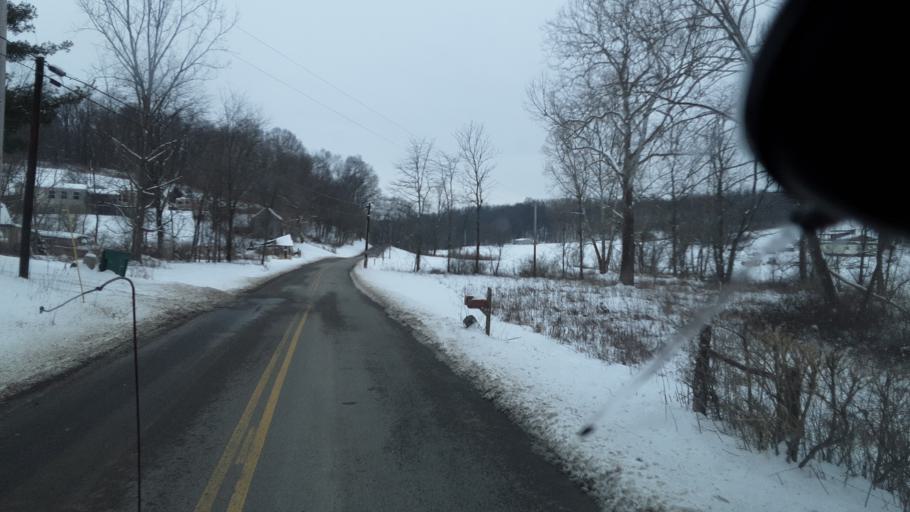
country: US
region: Ohio
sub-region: Perry County
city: Somerset
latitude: 39.9014
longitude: -82.2277
